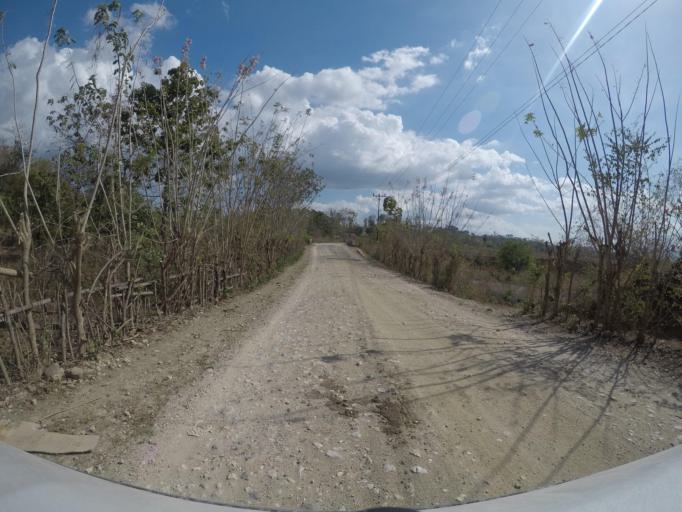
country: TL
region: Bobonaro
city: Maliana
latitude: -8.9971
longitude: 125.1985
